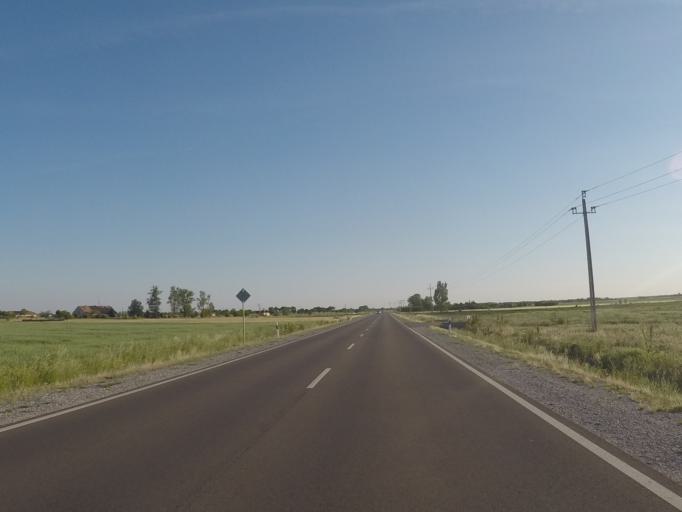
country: HU
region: Heves
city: Besenyotelek
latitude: 47.6902
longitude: 20.3922
